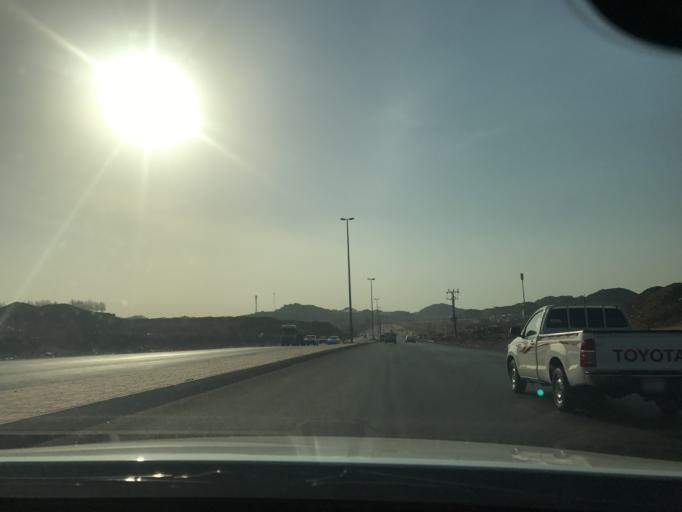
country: SA
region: Makkah
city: Jeddah
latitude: 21.4127
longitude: 39.4192
